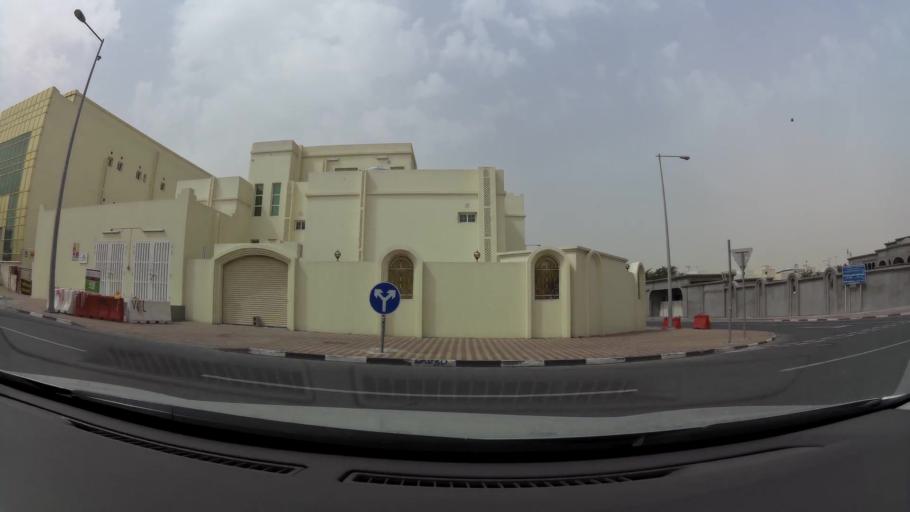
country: QA
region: Baladiyat ad Dawhah
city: Doha
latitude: 25.2569
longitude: 51.5477
